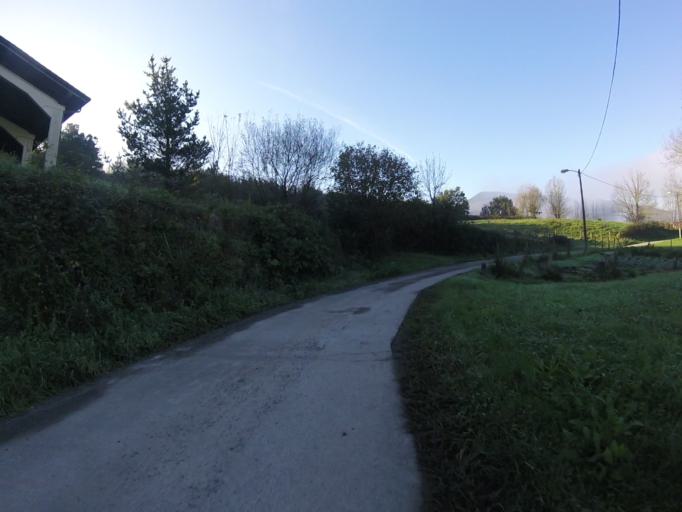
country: ES
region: Basque Country
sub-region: Provincia de Guipuzcoa
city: Usurbil
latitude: 43.2668
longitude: -2.0359
